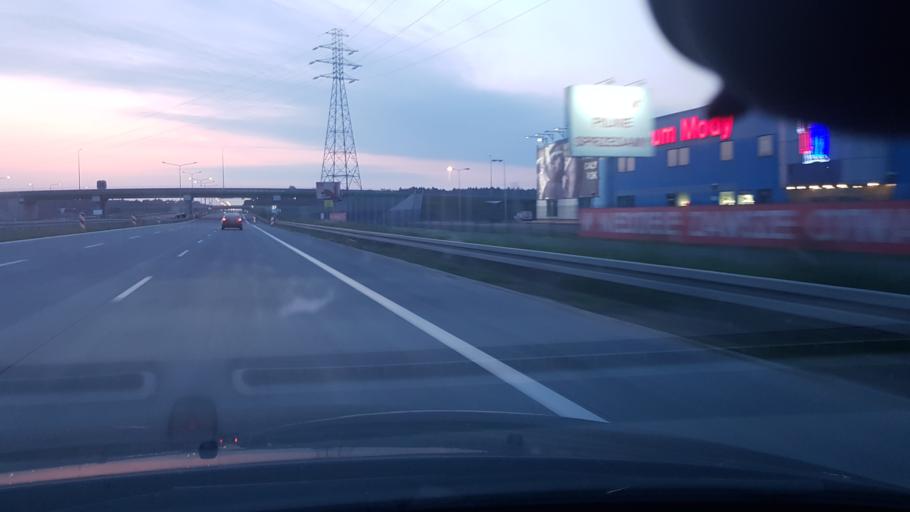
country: PL
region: Masovian Voivodeship
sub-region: Powiat pruszkowski
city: Nadarzyn
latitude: 52.1028
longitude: 20.8291
